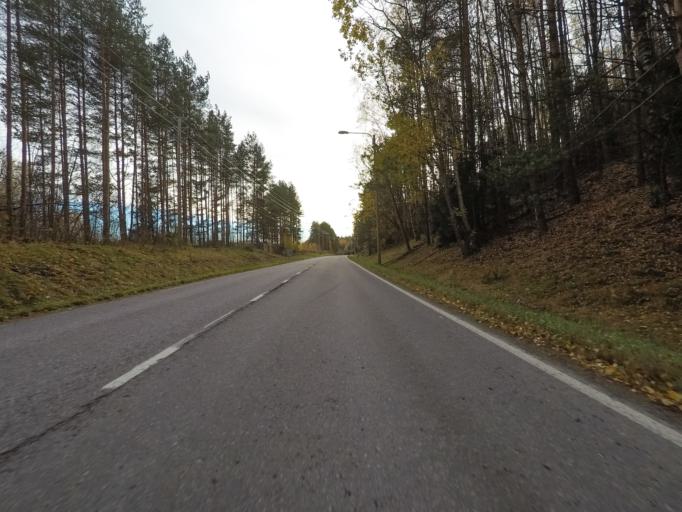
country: FI
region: Uusimaa
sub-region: Helsinki
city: Vantaa
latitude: 60.2642
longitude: 25.1404
